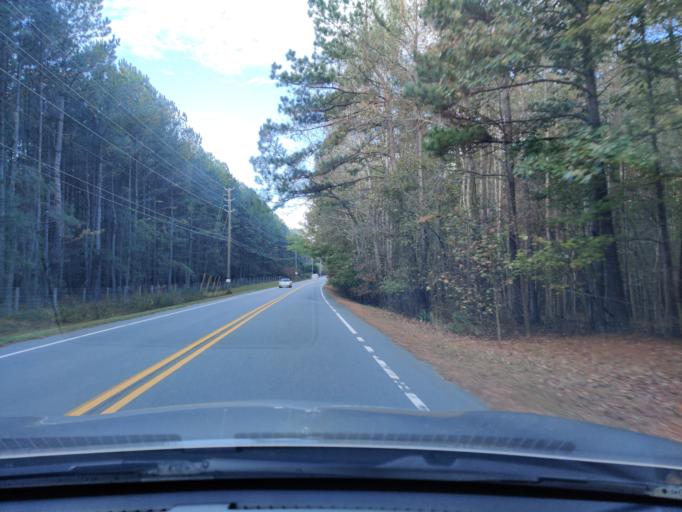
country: US
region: North Carolina
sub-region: Wake County
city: Morrisville
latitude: 35.9214
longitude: -78.7220
